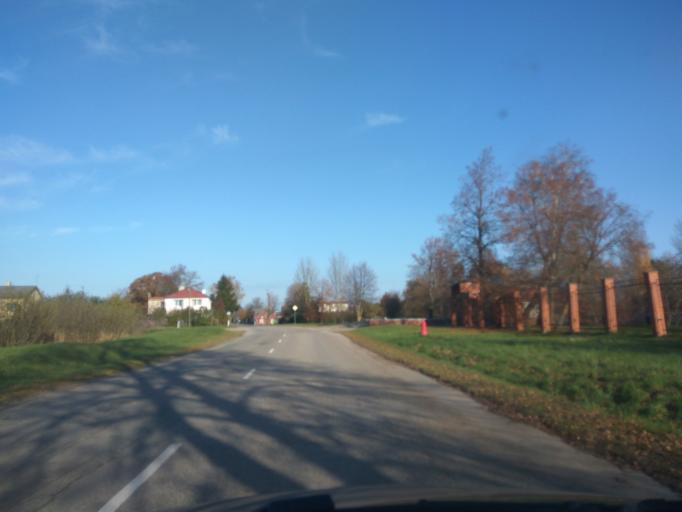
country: LV
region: Ventspils
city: Ventspils
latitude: 57.3704
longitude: 21.5679
